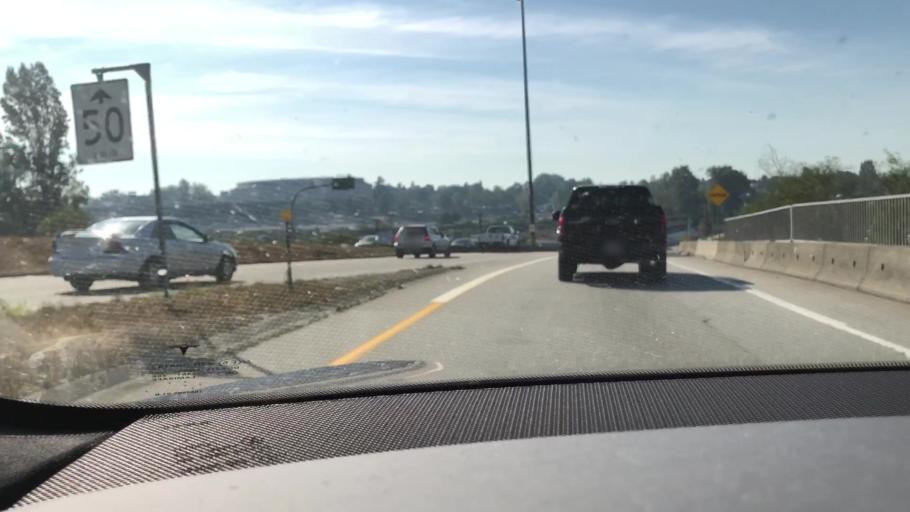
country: CA
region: British Columbia
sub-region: Fraser Valley Regional District
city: North Vancouver
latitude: 49.2877
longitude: -123.0334
